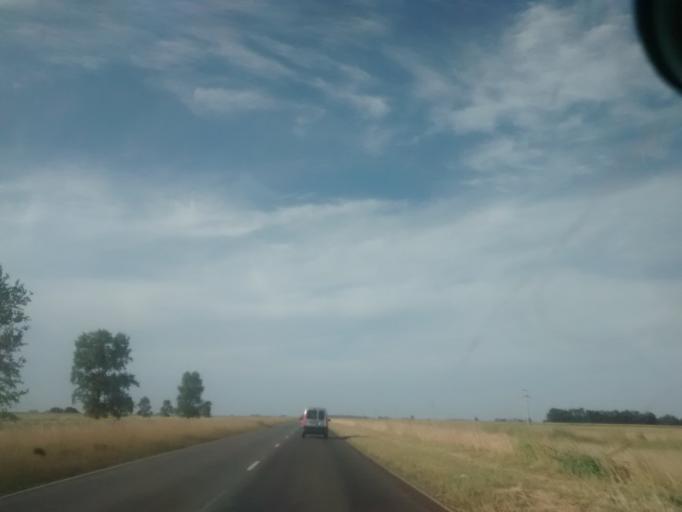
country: AR
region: Buenos Aires
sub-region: Partido de Ayacucho
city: Ayacucho
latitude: -37.1165
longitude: -58.5498
